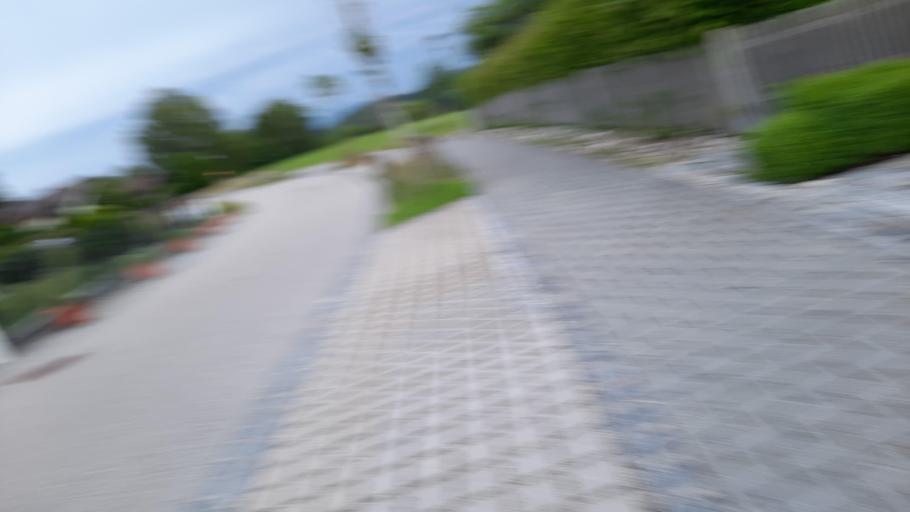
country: DE
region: Bavaria
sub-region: Upper Bavaria
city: Vagen
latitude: 47.8552
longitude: 11.8522
